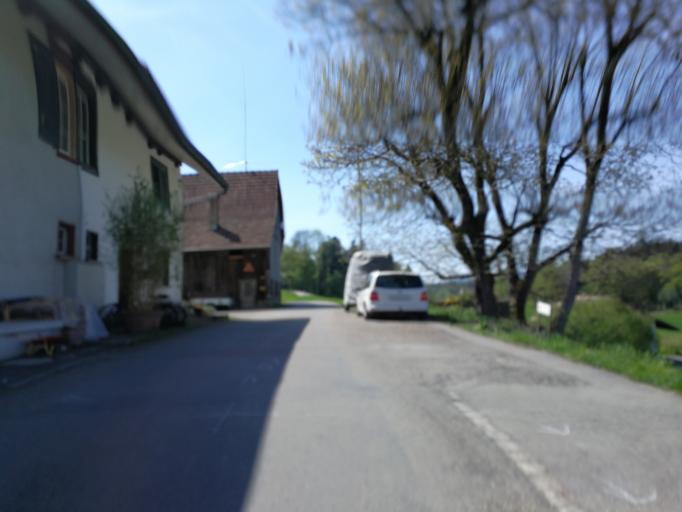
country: CH
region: Zurich
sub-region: Bezirk Hinwil
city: Bubikon
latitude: 47.2727
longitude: 8.8049
